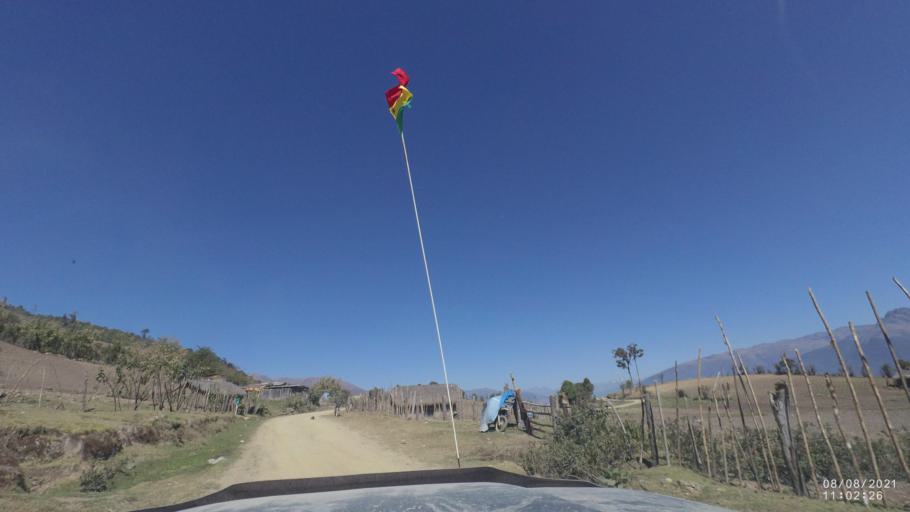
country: BO
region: Cochabamba
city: Colchani
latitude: -16.7532
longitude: -66.6873
